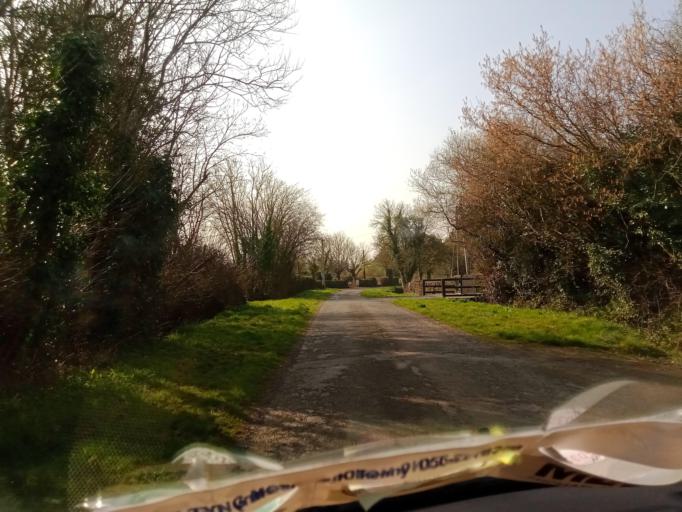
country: IE
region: Leinster
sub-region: Kilkenny
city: Callan
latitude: 52.5269
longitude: -7.3999
